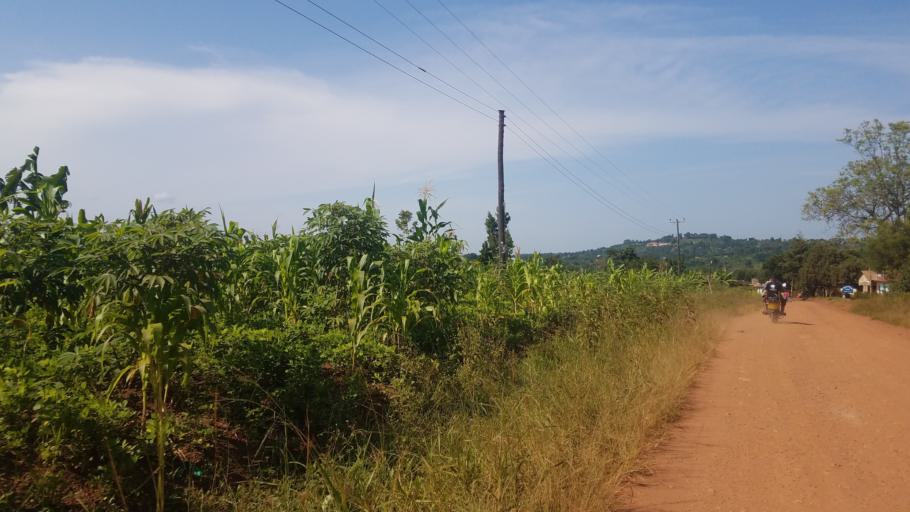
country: UG
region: Central Region
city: Masaka
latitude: -0.3099
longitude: 31.6821
